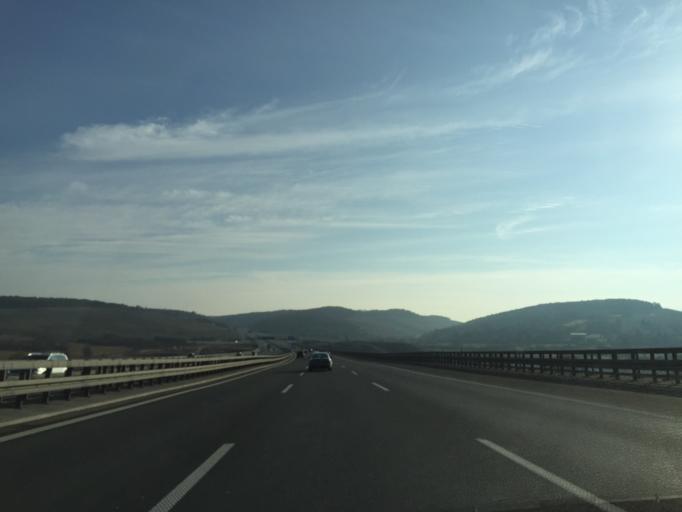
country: DE
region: Bavaria
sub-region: Regierungsbezirk Unterfranken
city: Eibelstadt
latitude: 49.7387
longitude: 9.9841
